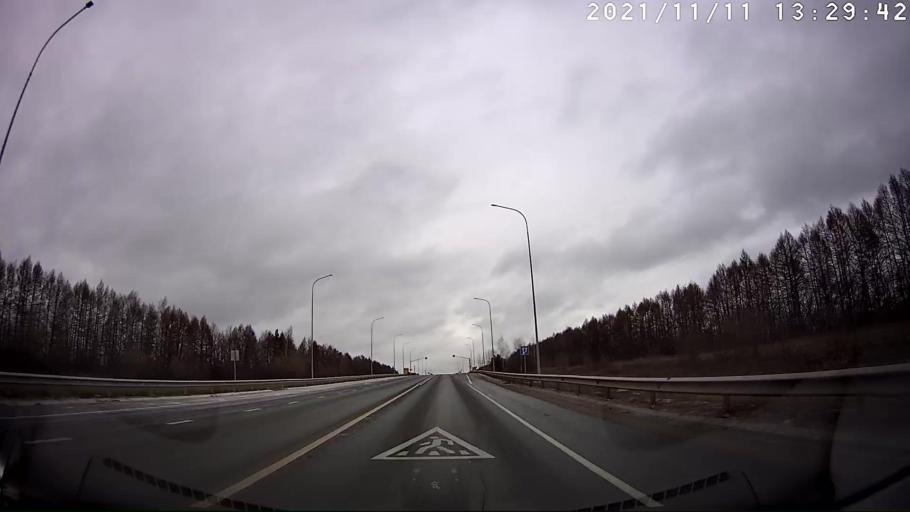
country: RU
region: Chuvashia
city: Komsomol'skoye
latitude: 55.3137
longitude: 47.5582
